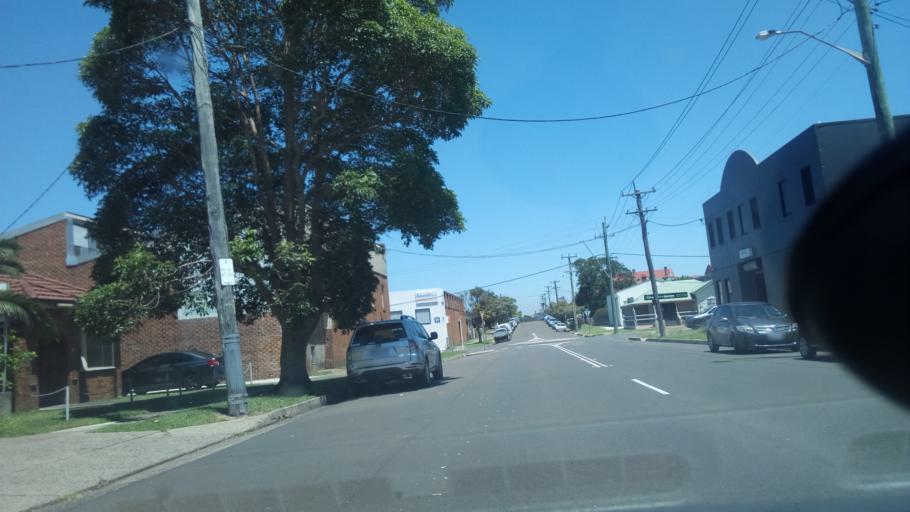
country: AU
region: New South Wales
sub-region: Wollongong
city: Wollongong
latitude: -34.4287
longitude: 150.8904
